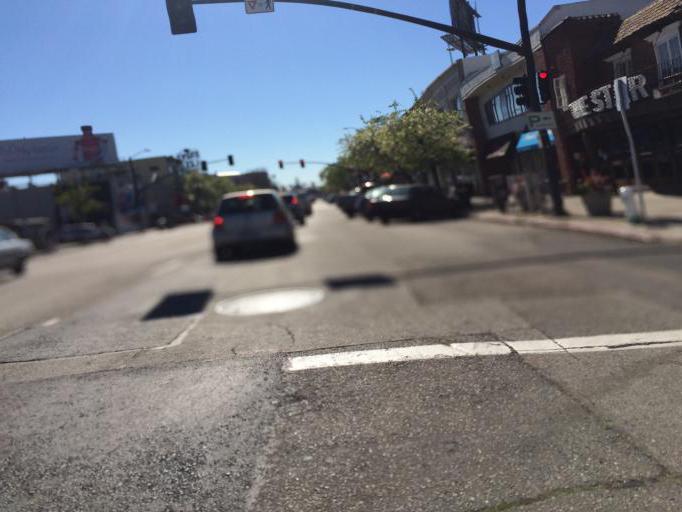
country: US
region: California
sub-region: Alameda County
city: Piedmont
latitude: 37.8144
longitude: -122.2462
